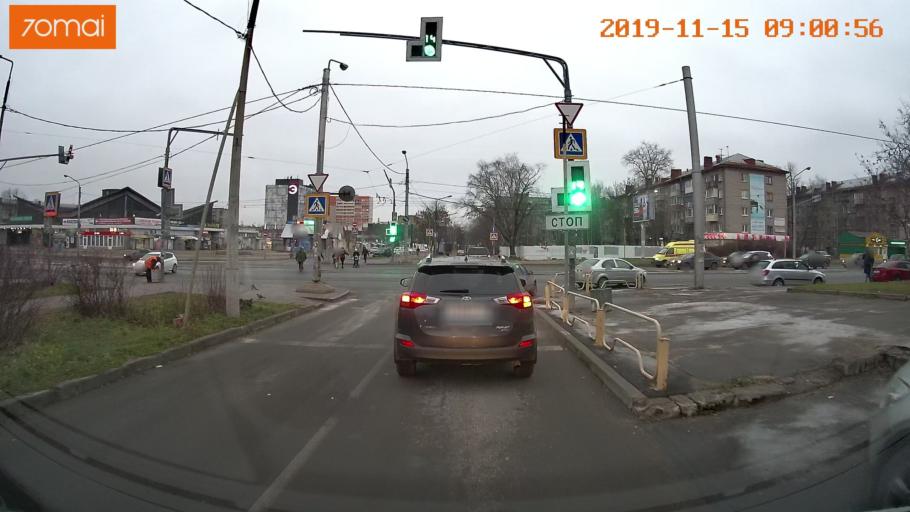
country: RU
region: Vologda
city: Cherepovets
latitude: 59.1301
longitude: 37.9249
